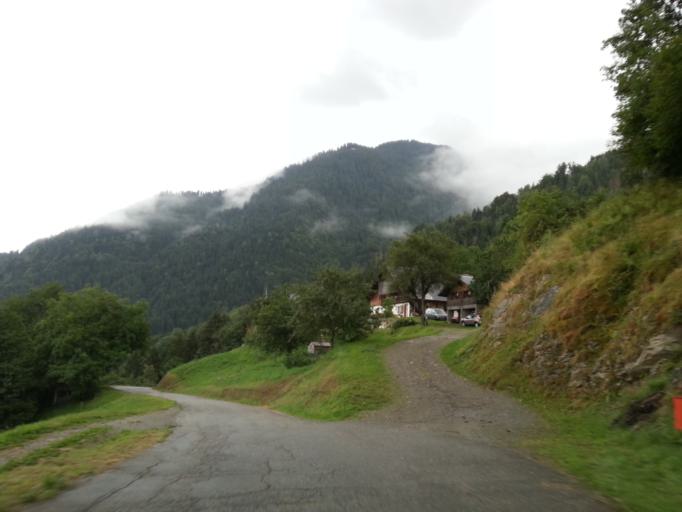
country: FR
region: Rhone-Alpes
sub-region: Departement de la Savoie
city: Marthod
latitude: 45.7073
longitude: 6.4659
